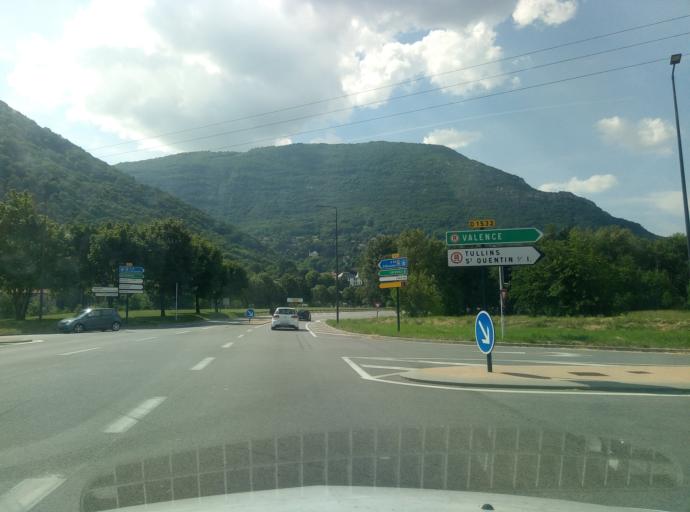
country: FR
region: Rhone-Alpes
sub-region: Departement de l'Isere
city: Veurey-Voroize
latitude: 45.2682
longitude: 5.6204
